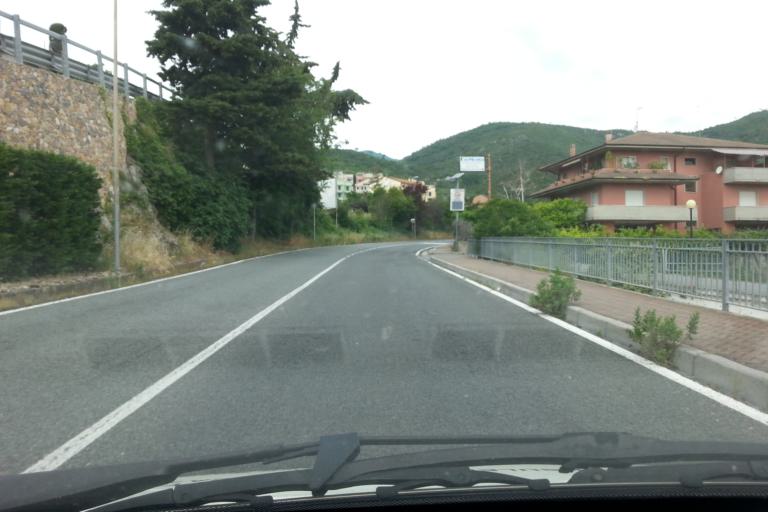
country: IT
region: Liguria
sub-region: Provincia di Savona
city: Pietra Ligure
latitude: 44.1464
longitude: 8.2706
